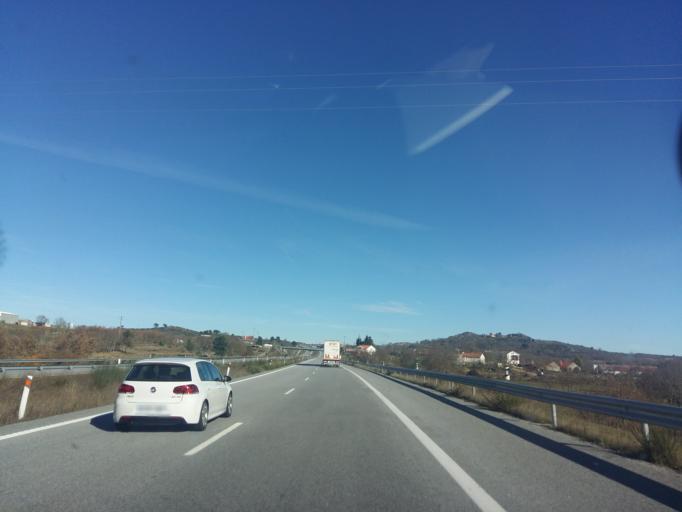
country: PT
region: Guarda
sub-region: Guarda
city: Sequeira
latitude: 40.5831
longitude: -7.1548
